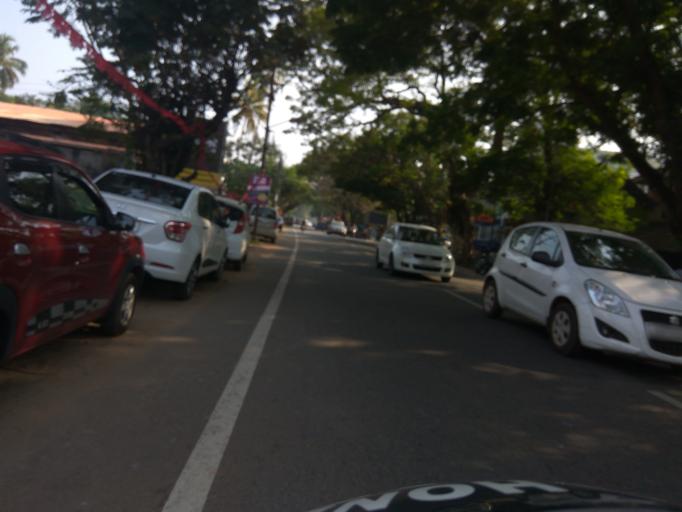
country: IN
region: Kerala
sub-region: Kozhikode
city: Kozhikode
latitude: 11.2807
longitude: 75.7704
